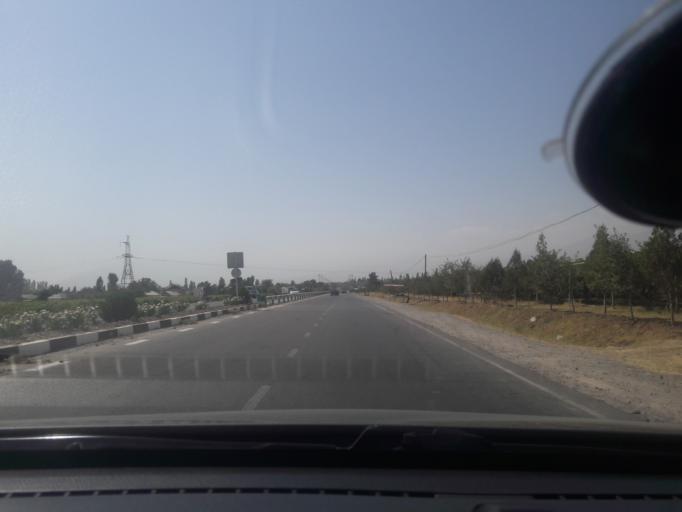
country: TJ
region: Republican Subordination
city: Hisor
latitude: 38.5601
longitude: 68.4541
